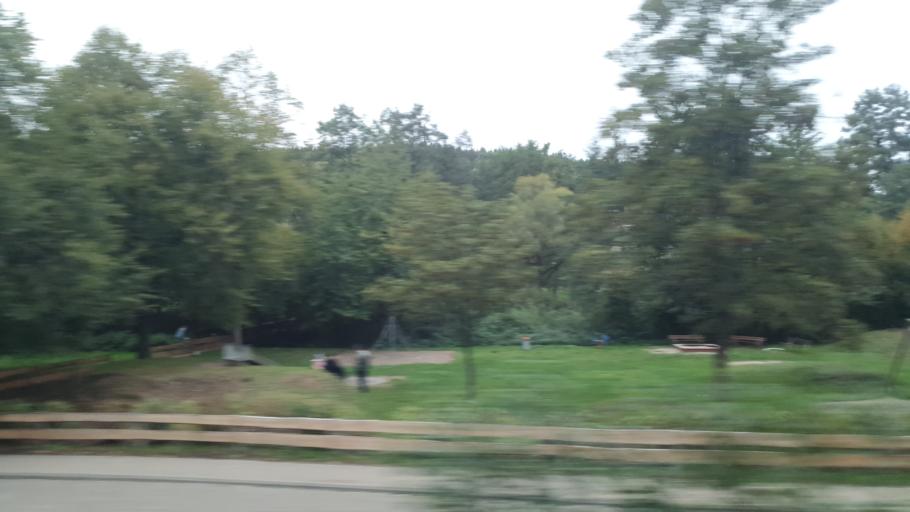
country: DE
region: Saarland
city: Kirkel
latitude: 49.2444
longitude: 7.2008
